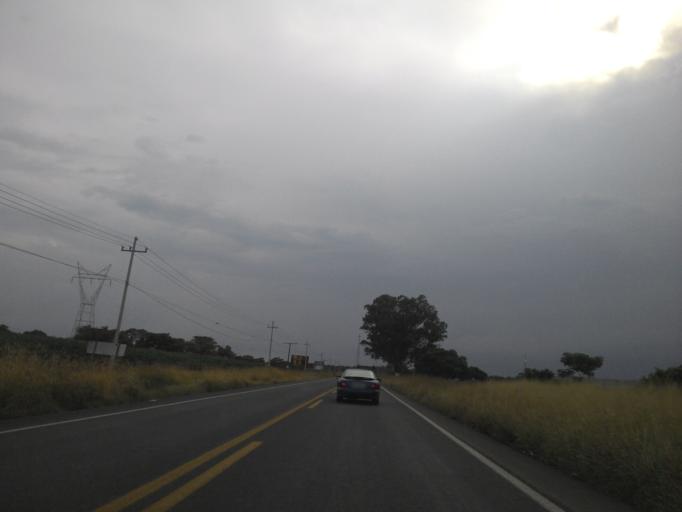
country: MX
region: Jalisco
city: Acatic
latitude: 20.7036
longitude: -102.9671
